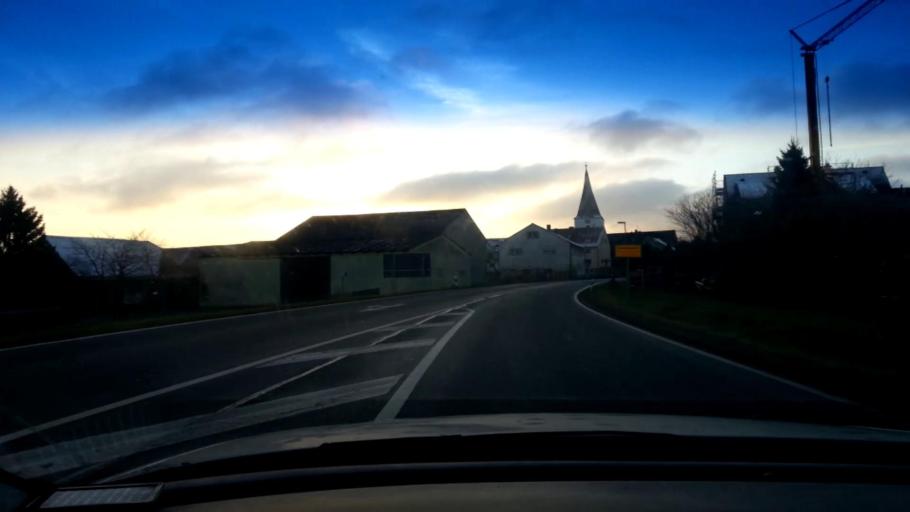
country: DE
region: Bavaria
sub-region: Upper Franconia
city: Frensdorf
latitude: 49.7936
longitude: 10.8889
